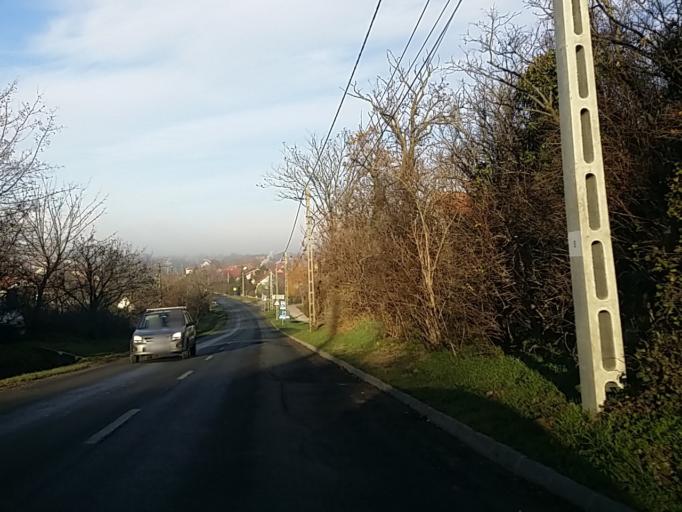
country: HU
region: Pest
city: Telki
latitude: 47.5478
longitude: 18.8263
